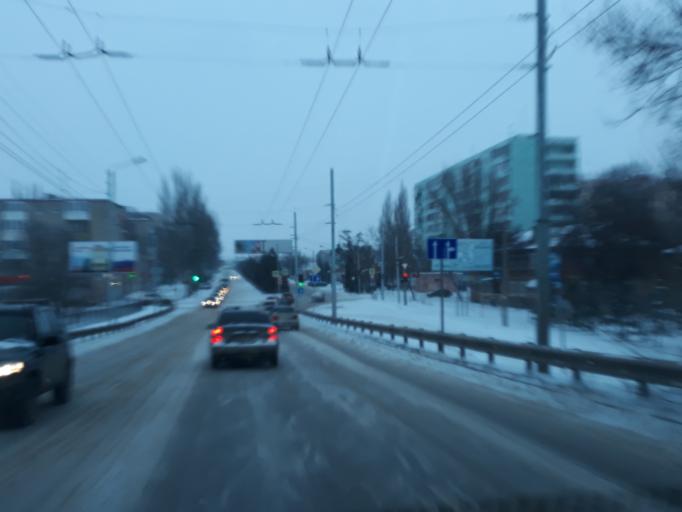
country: RU
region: Rostov
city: Taganrog
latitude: 47.2666
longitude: 38.9241
